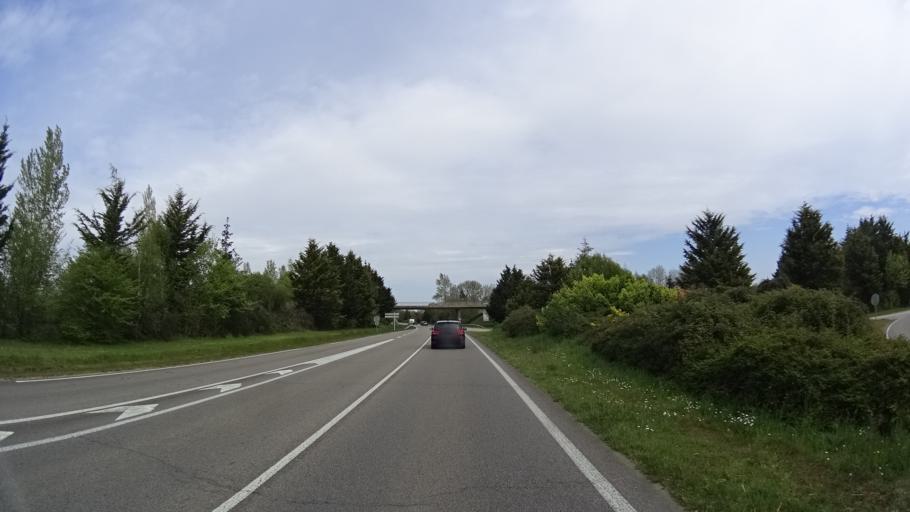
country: FR
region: Pays de la Loire
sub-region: Departement de la Loire-Atlantique
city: Port-Saint-Pere
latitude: 47.1193
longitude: -1.7662
